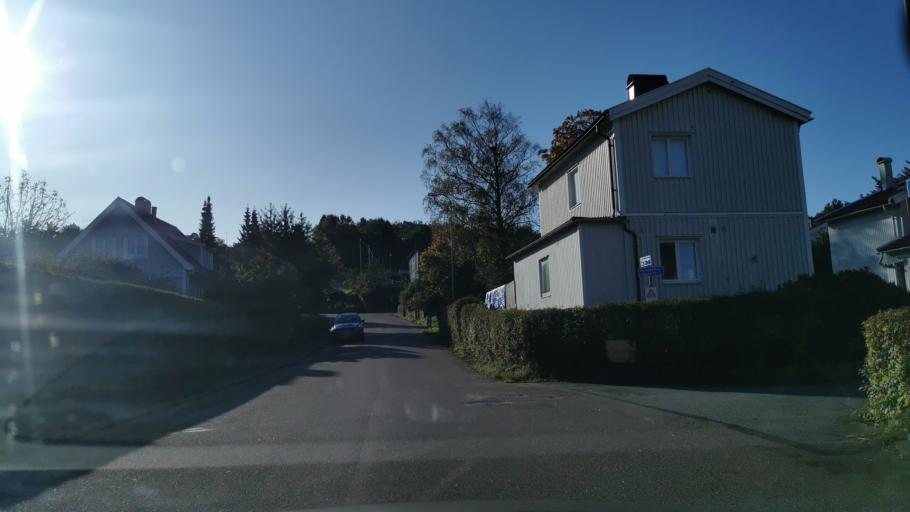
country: SE
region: Vaestra Goetaland
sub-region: Goteborg
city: Eriksbo
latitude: 57.7291
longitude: 12.0555
